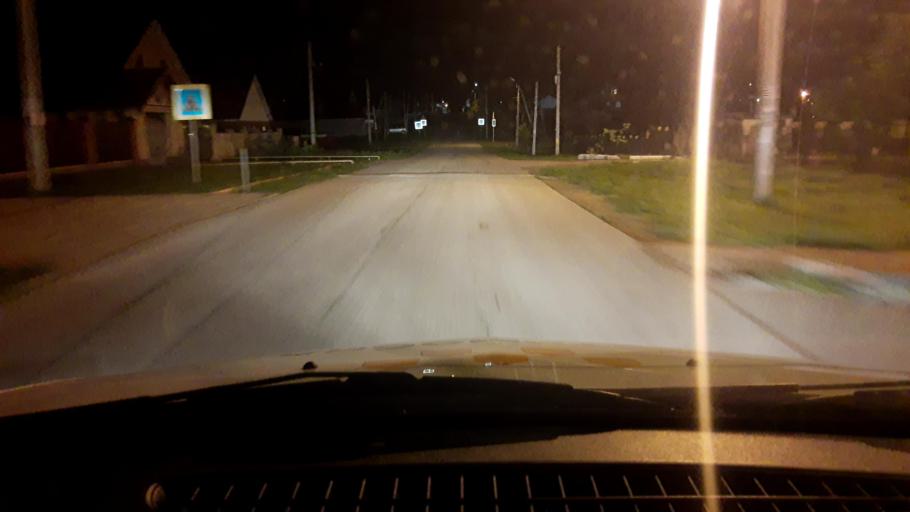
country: RU
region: Bashkortostan
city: Avdon
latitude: 54.6551
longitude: 55.7360
